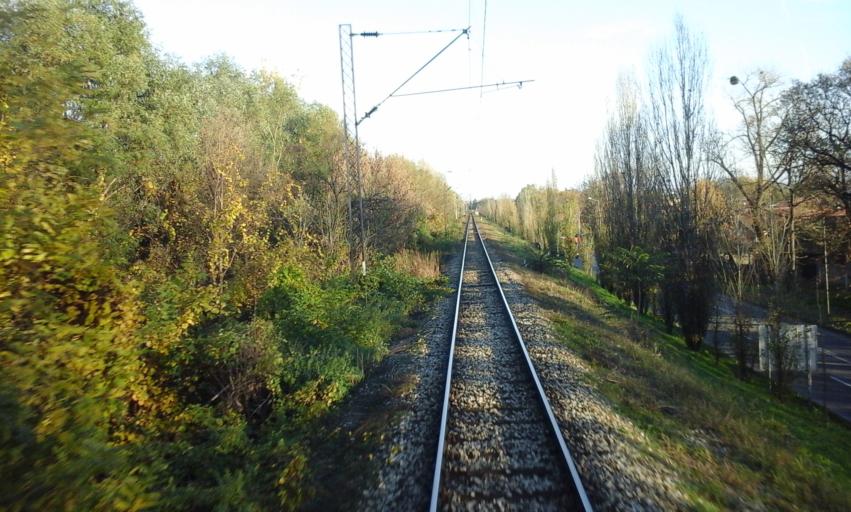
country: RS
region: Autonomna Pokrajina Vojvodina
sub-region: Juznobacki Okrug
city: Petrovaradin
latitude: 45.2585
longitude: 19.8684
